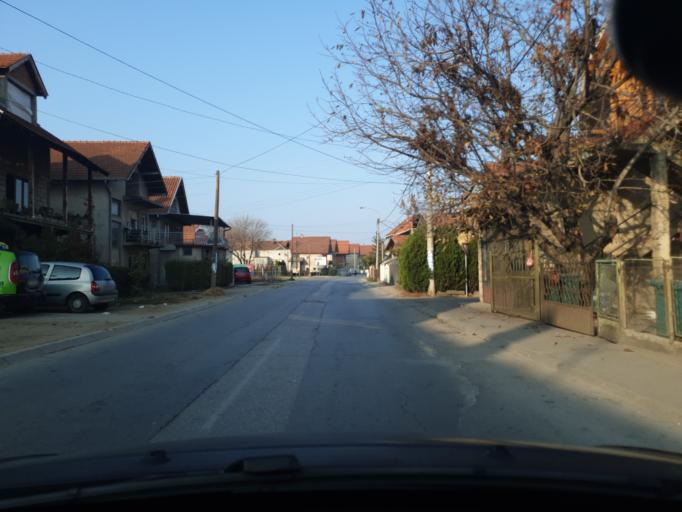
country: RS
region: Central Serbia
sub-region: Jablanicki Okrug
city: Leskovac
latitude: 42.9947
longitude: 21.9320
